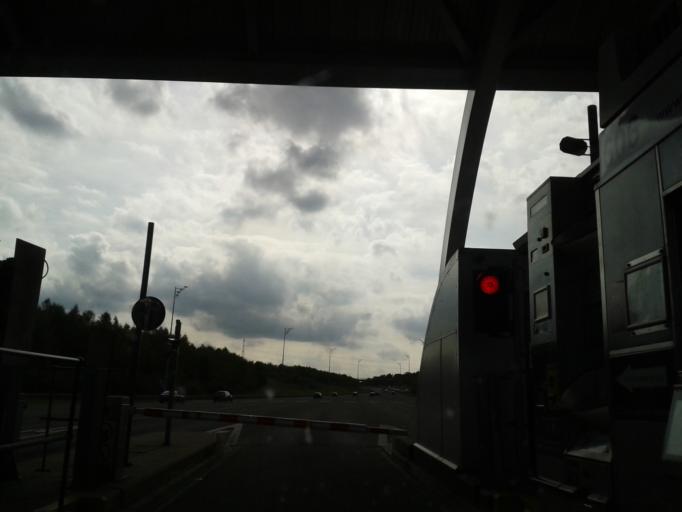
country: GB
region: England
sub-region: Staffordshire
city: Shenstone
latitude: 52.6231
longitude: -1.8007
